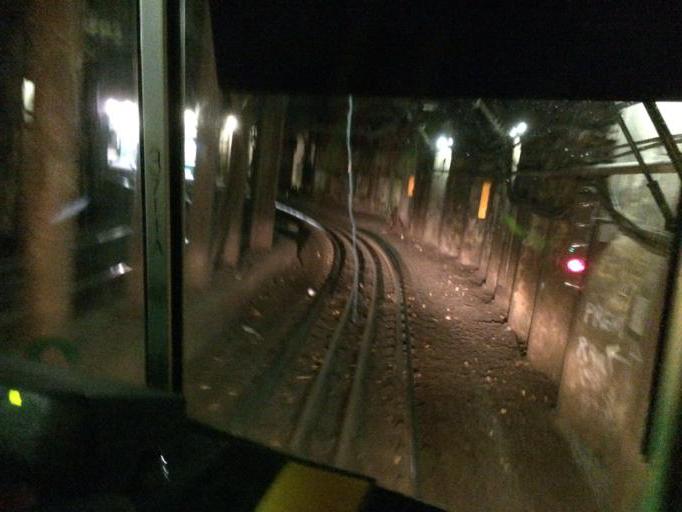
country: US
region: Massachusetts
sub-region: Suffolk County
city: Boston
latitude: 42.3502
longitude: -71.0726
